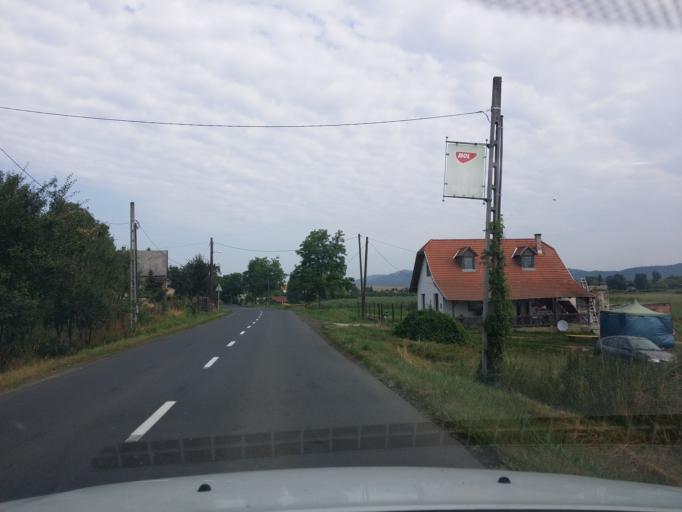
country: HU
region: Nograd
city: Bercel
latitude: 47.8397
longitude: 19.3893
